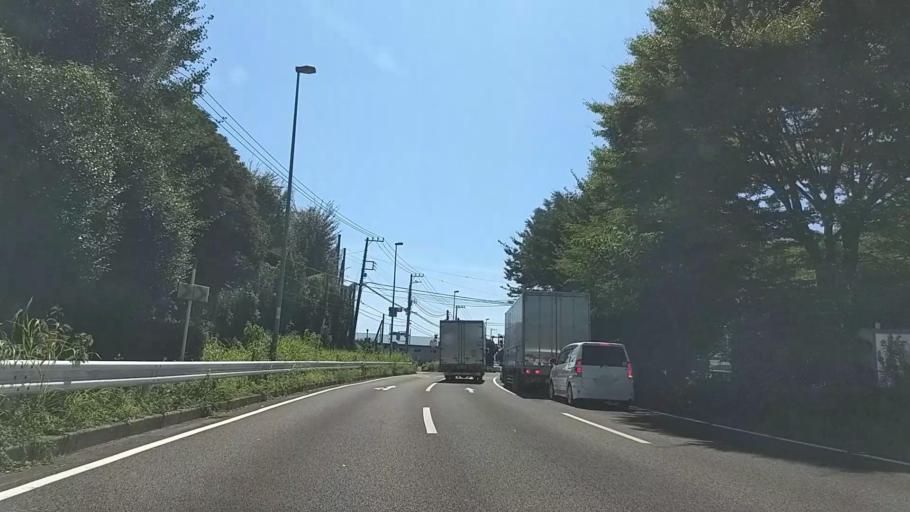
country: JP
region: Kanagawa
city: Zama
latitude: 35.5414
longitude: 139.3610
